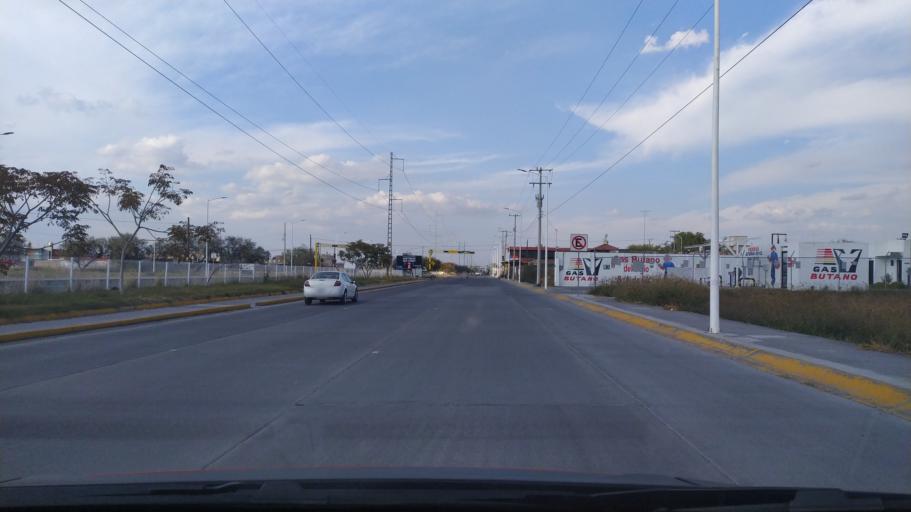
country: MX
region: Guanajuato
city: San Francisco del Rincon
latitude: 21.0126
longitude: -101.8698
